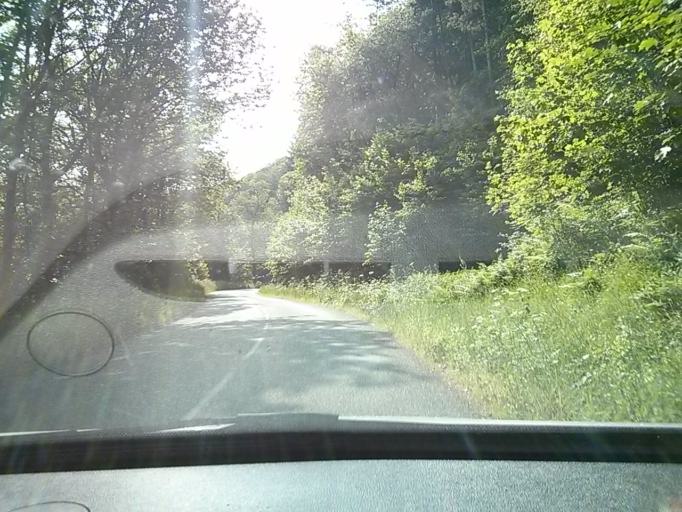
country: FR
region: Rhone-Alpes
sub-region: Departement de la Loire
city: Saint-Chamond
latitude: 45.4248
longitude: 4.5205
